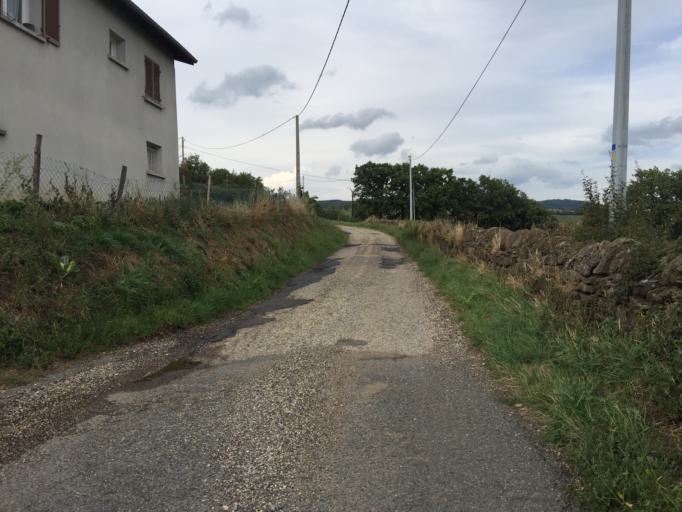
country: FR
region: Rhone-Alpes
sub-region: Departement de la Loire
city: Sorbiers
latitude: 45.4869
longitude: 4.4739
